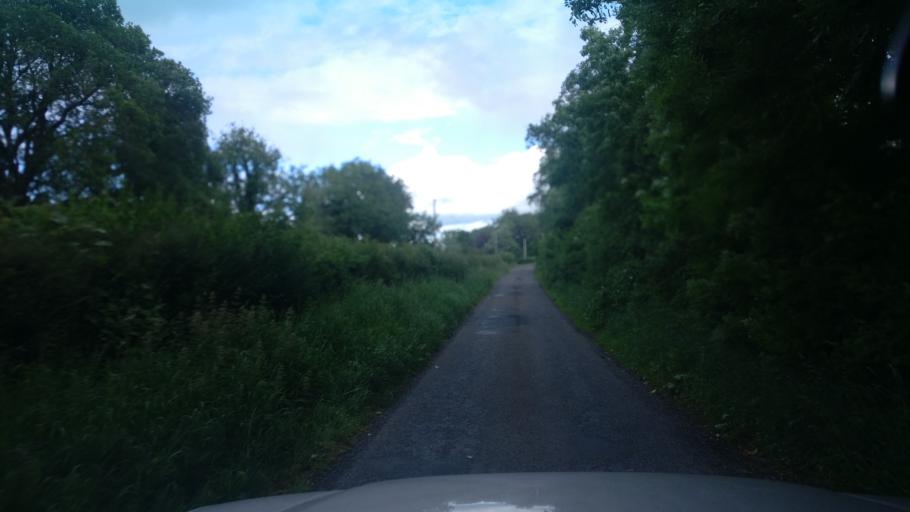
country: IE
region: Connaught
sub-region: County Galway
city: Portumna
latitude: 53.1988
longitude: -8.3540
